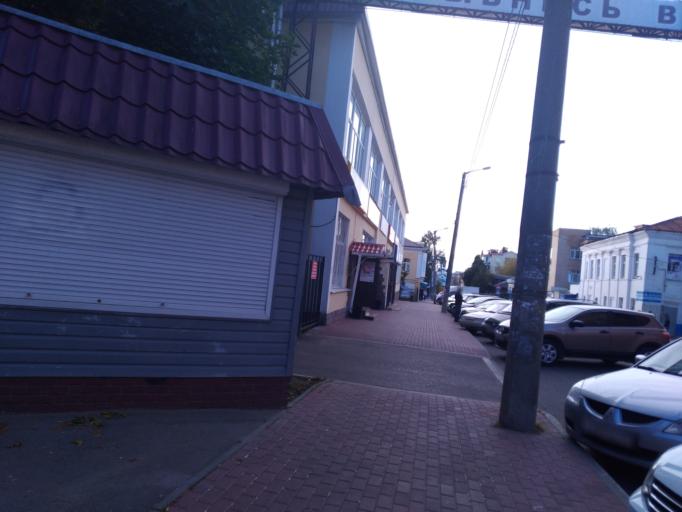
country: RU
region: Kaluga
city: Kaluga
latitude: 54.5113
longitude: 36.2561
